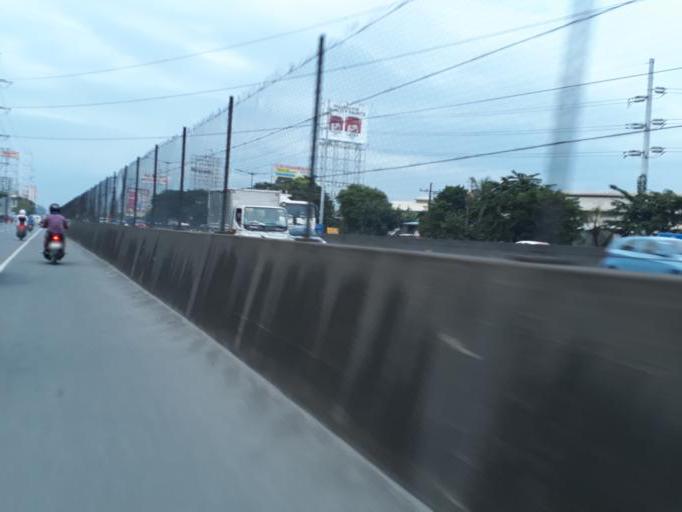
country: PH
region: Calabarzon
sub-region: Province of Rizal
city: Valenzuela
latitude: 14.7016
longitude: 120.9964
